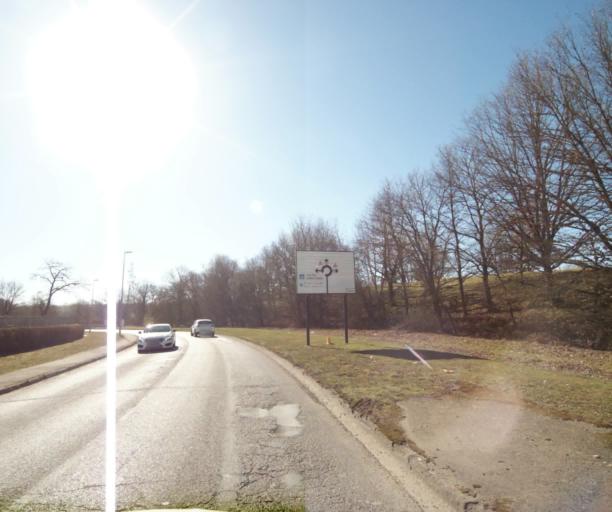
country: FR
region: Lorraine
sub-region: Departement de Meurthe-et-Moselle
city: Fleville-devant-Nancy
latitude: 48.6116
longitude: 6.1907
